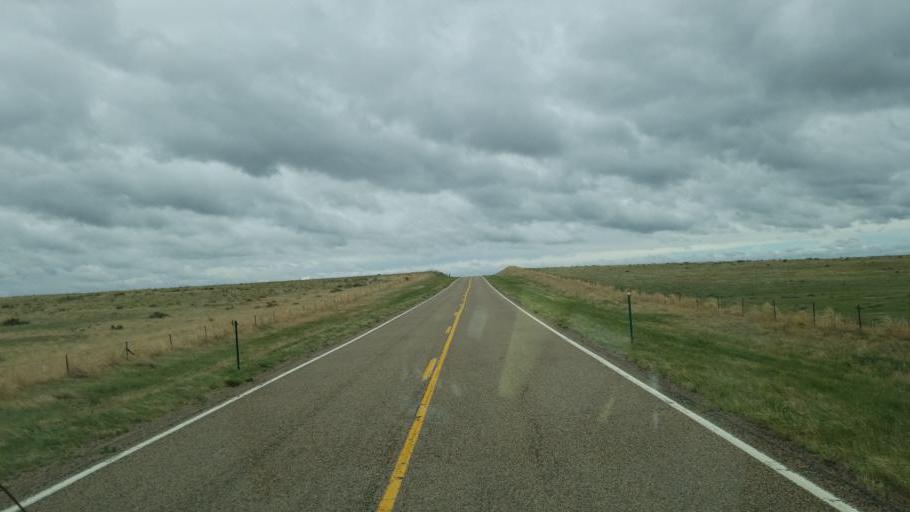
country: US
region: Colorado
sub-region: Lincoln County
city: Hugo
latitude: 38.8508
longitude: -103.5792
